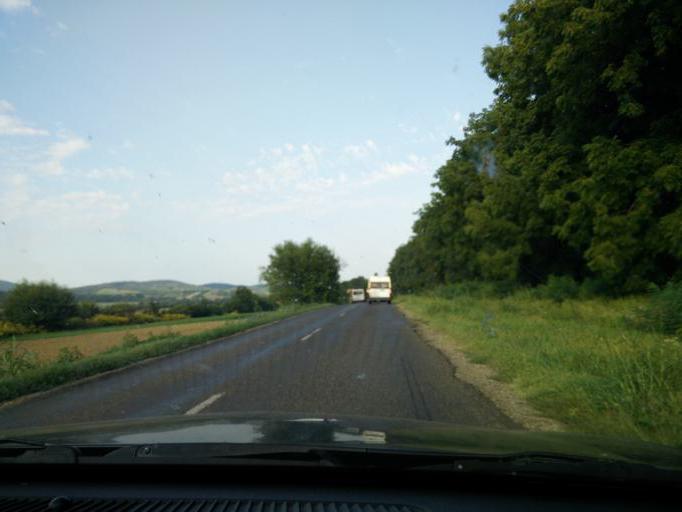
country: HU
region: Tolna
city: Nagymanyok
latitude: 46.2811
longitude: 18.4281
